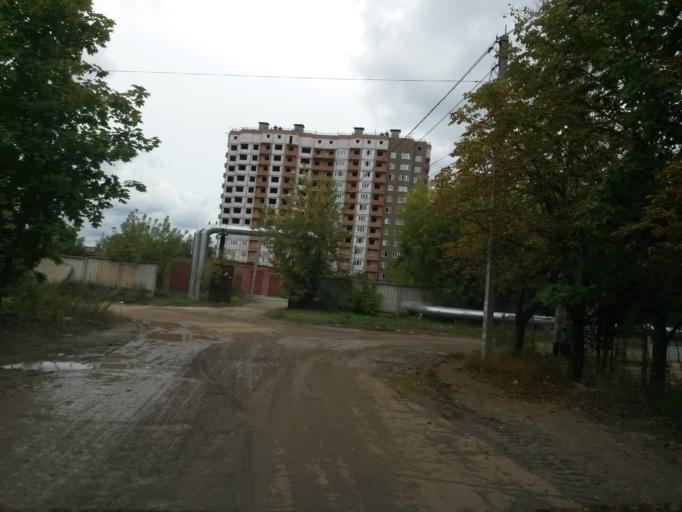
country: RU
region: Moskovskaya
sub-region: Chekhovskiy Rayon
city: Chekhov
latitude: 55.1443
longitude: 37.4793
